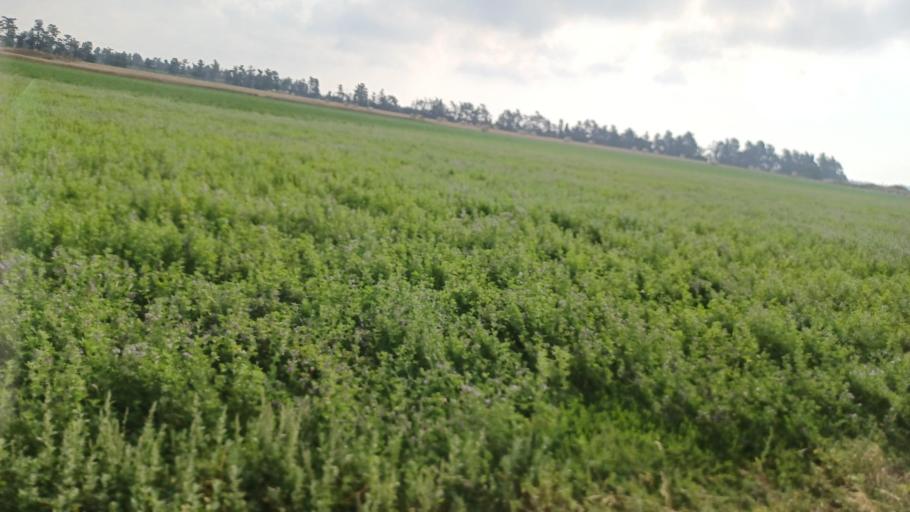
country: CY
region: Larnaka
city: Meneou
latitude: 34.8485
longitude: 33.5968
